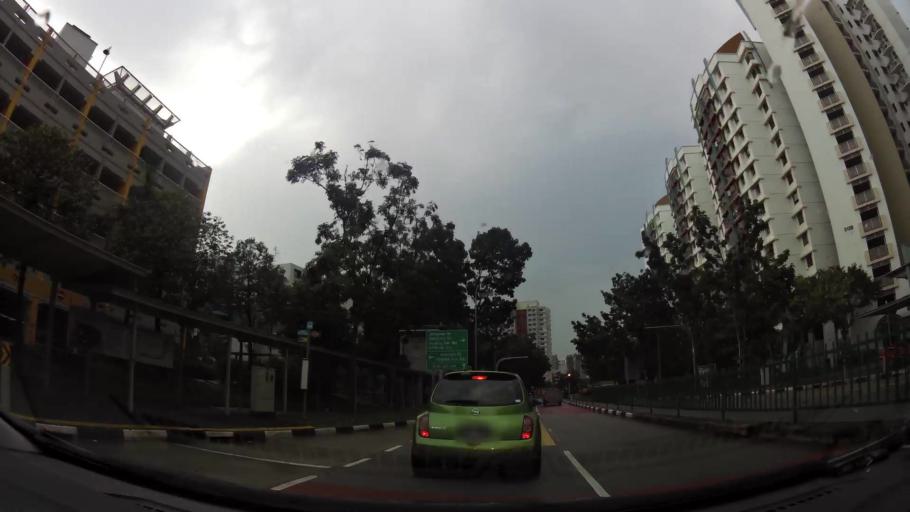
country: MY
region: Johor
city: Kampung Pasir Gudang Baru
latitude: 1.3908
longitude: 103.8883
